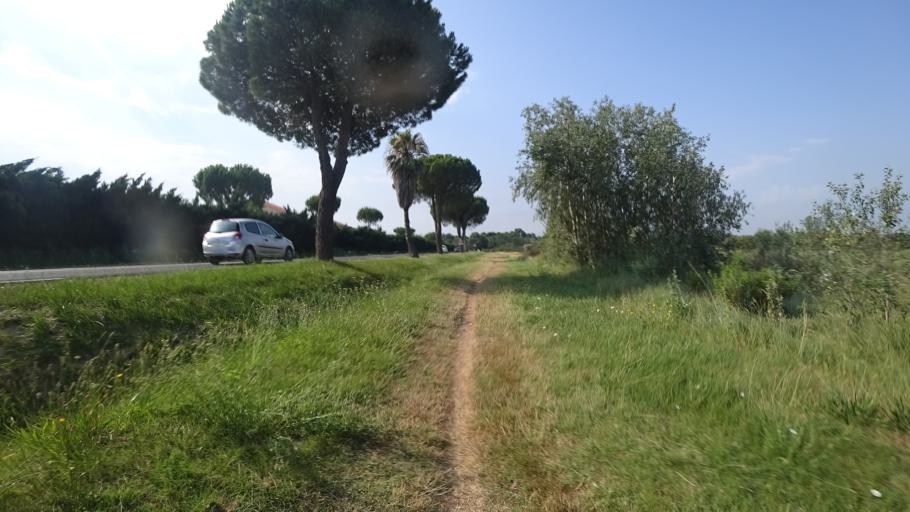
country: FR
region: Languedoc-Roussillon
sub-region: Departement des Pyrenees-Orientales
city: Canet-en-Roussillon
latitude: 42.6935
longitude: 3.0254
